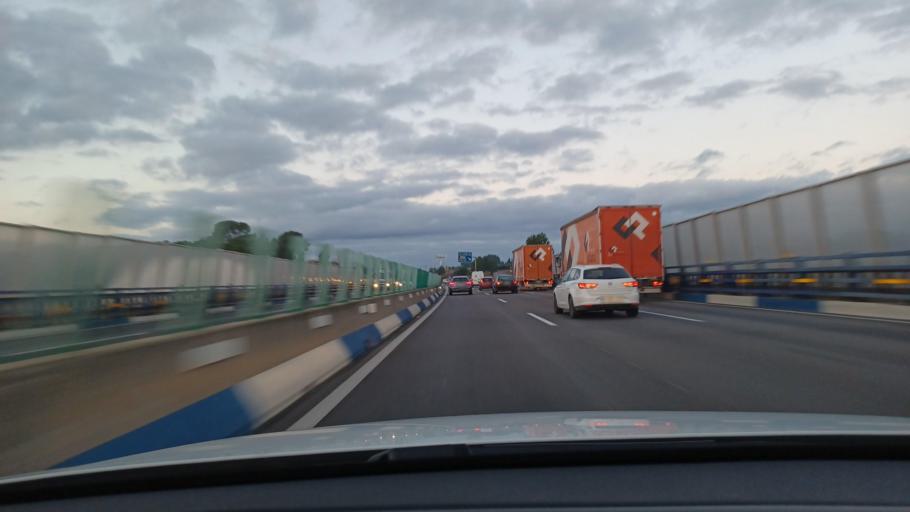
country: ES
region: Valencia
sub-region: Provincia de Valencia
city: Manises
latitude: 39.5117
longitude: -0.5014
